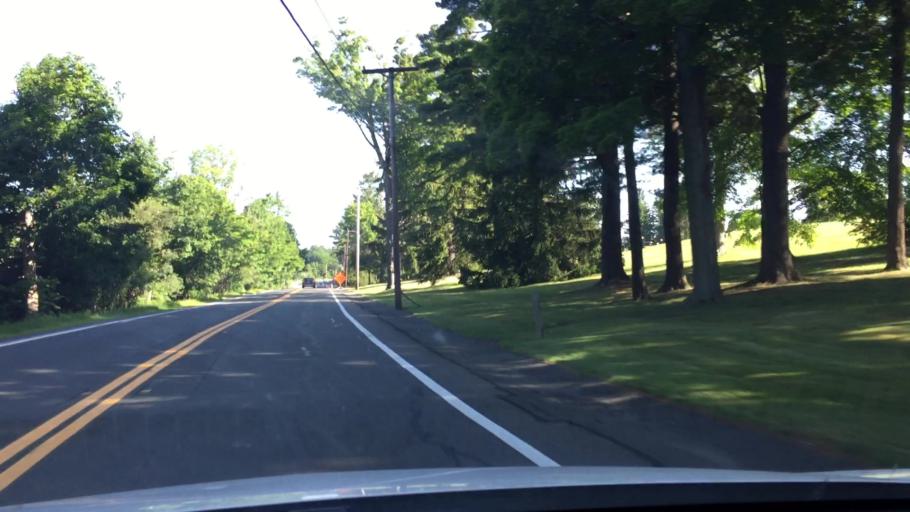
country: US
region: Massachusetts
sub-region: Berkshire County
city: Lenox
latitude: 42.3385
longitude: -73.2680
